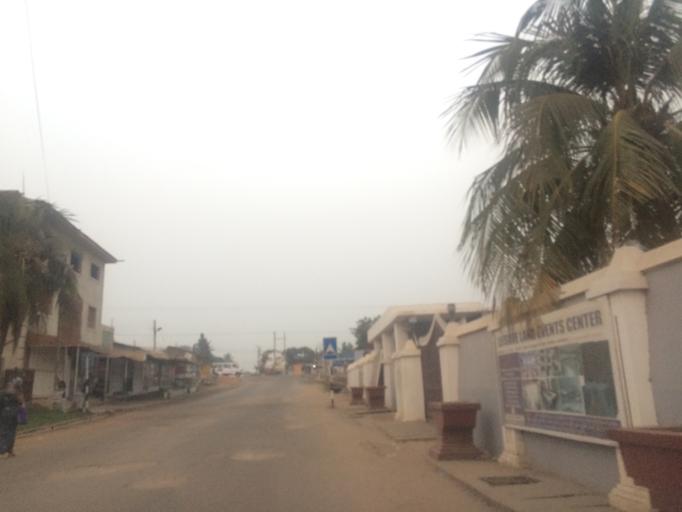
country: GH
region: Greater Accra
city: Teshi Old Town
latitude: 5.5979
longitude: -0.1013
